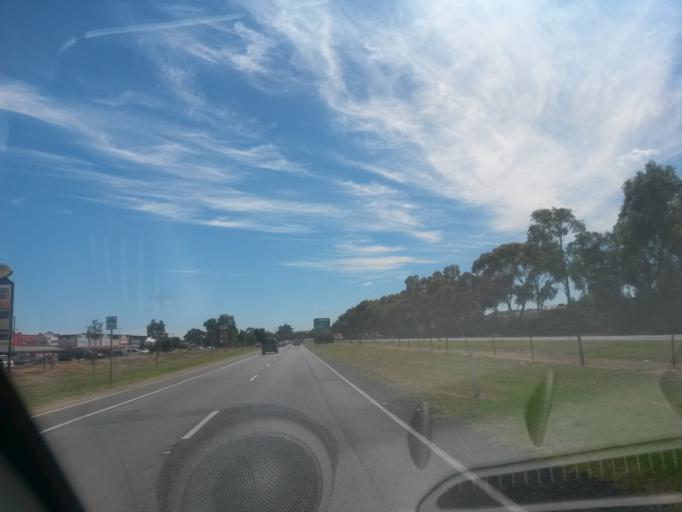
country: AU
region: South Australia
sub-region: Salisbury
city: Salisbury
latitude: -34.7962
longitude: 138.6430
